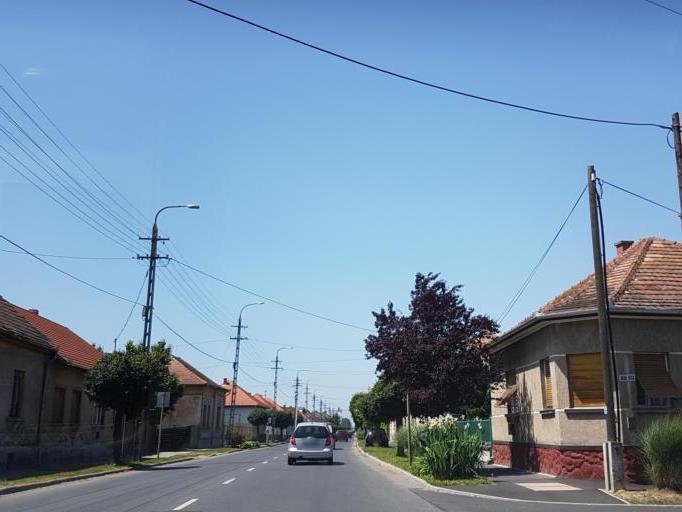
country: HU
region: Zala
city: Zalaegerszeg
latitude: 46.8481
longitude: 16.8258
